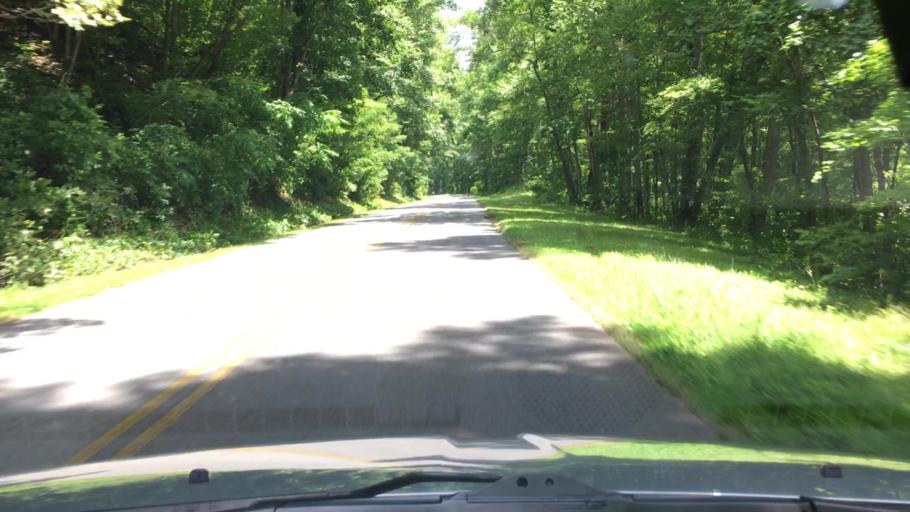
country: US
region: North Carolina
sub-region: Buncombe County
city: Asheville
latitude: 35.6338
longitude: -82.4956
